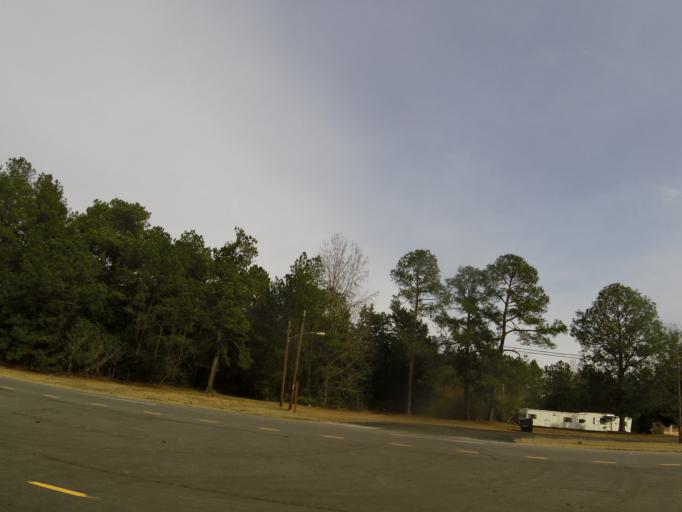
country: US
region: Alabama
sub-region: Dale County
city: Ozark
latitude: 31.4962
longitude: -85.6929
